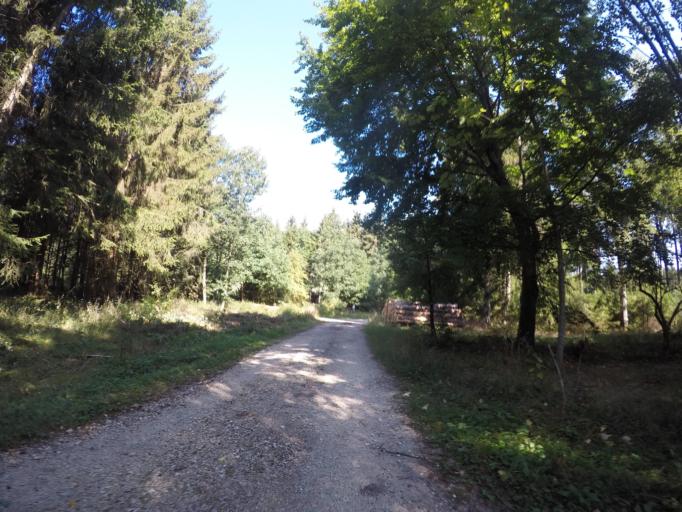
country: DE
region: Baden-Wuerttemberg
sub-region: Tuebingen Region
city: Beimerstetten
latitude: 48.4811
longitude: 9.9656
